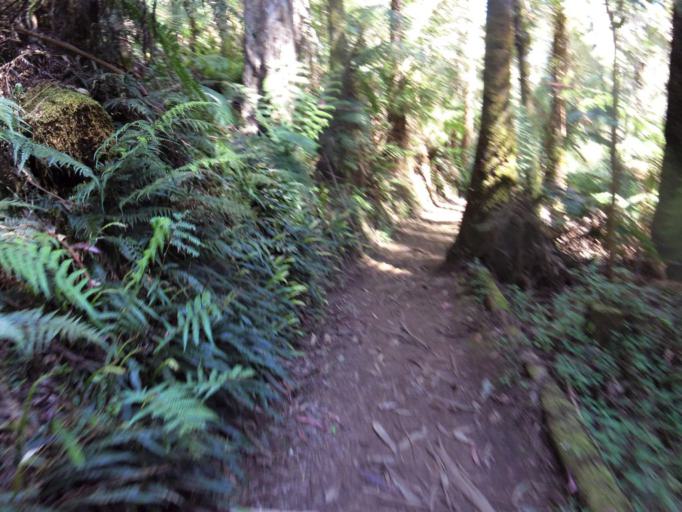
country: AU
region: Victoria
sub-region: Baw Baw
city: Warragul
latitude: -37.8438
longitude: 146.0482
